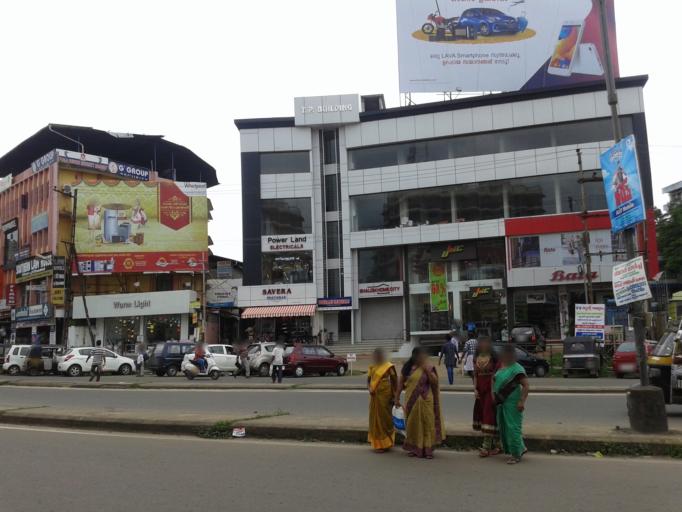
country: IN
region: Kerala
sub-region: Kozhikode
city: Kozhikode
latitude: 11.2528
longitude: 75.7834
